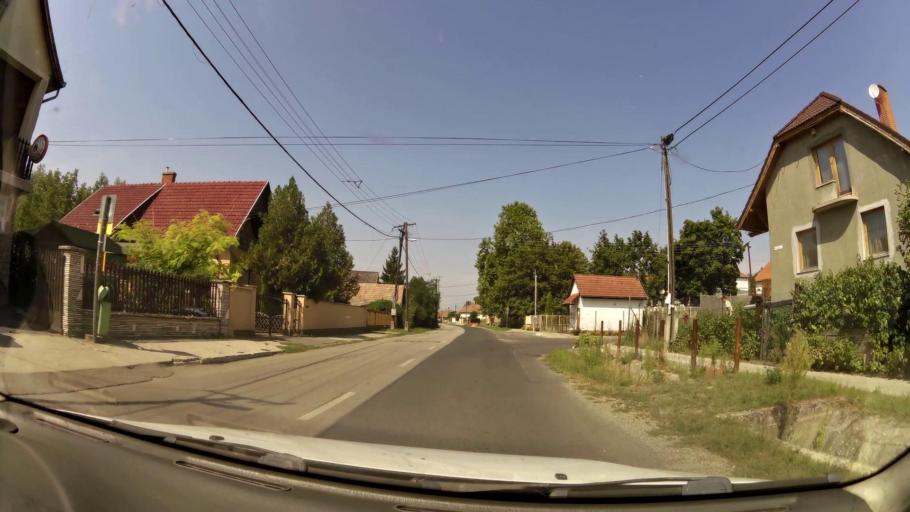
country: HU
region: Pest
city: Tapiosag
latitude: 47.3991
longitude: 19.6291
